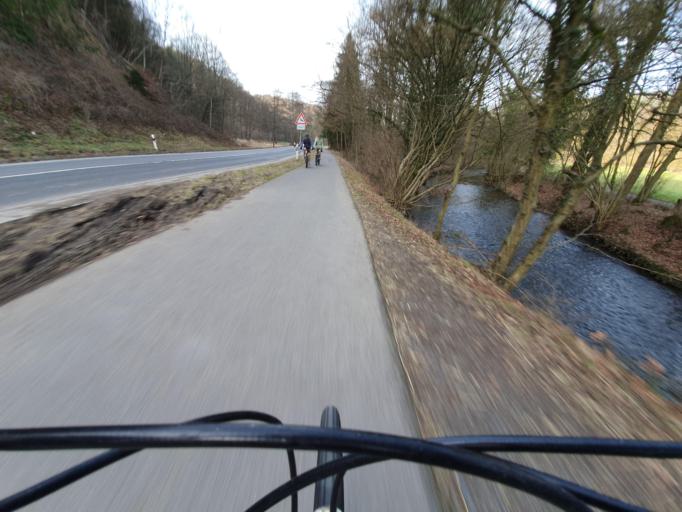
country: DE
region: North Rhine-Westphalia
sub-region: Regierungsbezirk Koln
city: Odenthal
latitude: 51.0435
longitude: 7.1236
